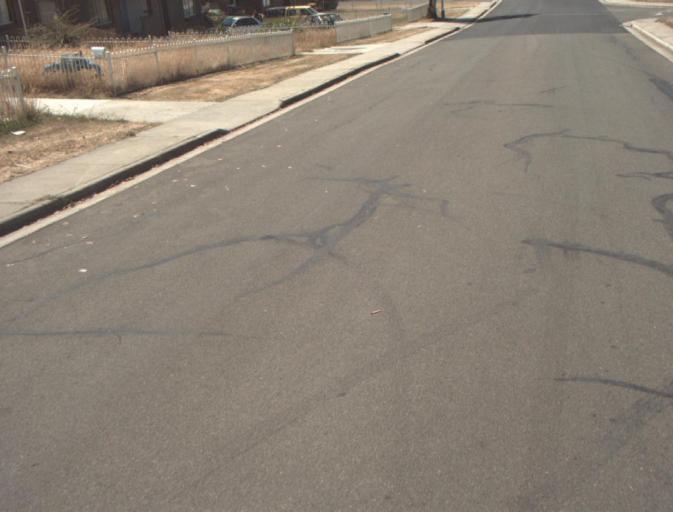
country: AU
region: Tasmania
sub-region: Launceston
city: Newstead
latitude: -41.4098
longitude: 147.1665
